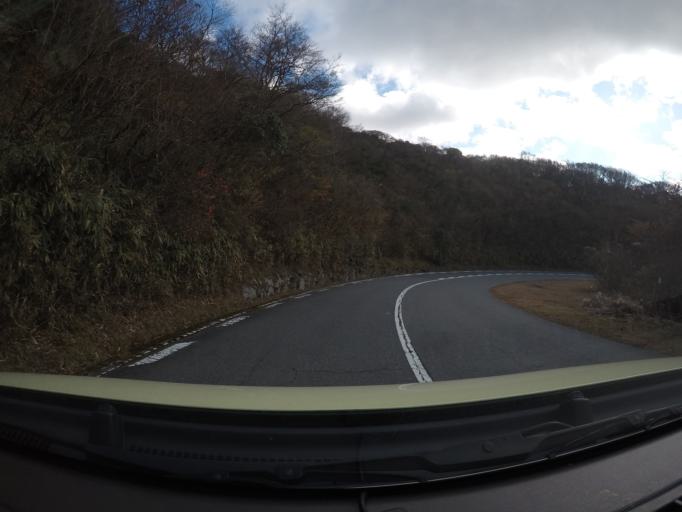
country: JP
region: Kanagawa
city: Hakone
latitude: 35.2110
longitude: 138.9875
